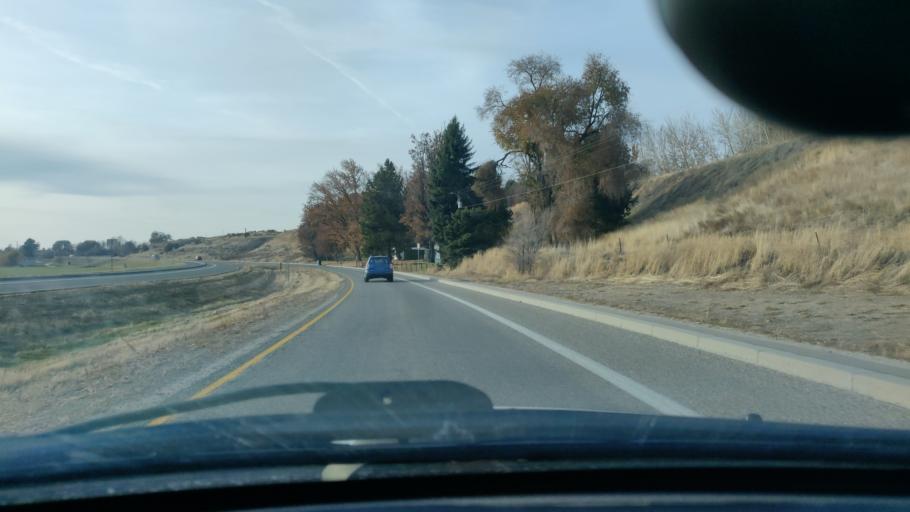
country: US
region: Idaho
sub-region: Ada County
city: Eagle
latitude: 43.6906
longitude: -116.3048
